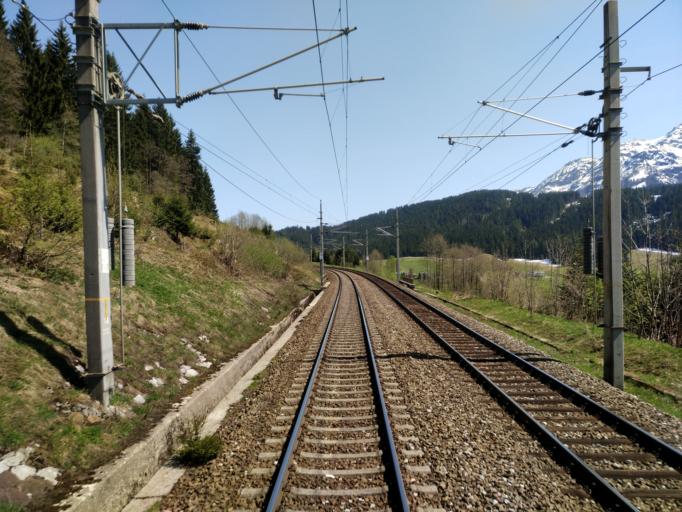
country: AT
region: Tyrol
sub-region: Politischer Bezirk Kitzbuhel
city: Hochfilzen
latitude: 47.4679
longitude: 12.5923
